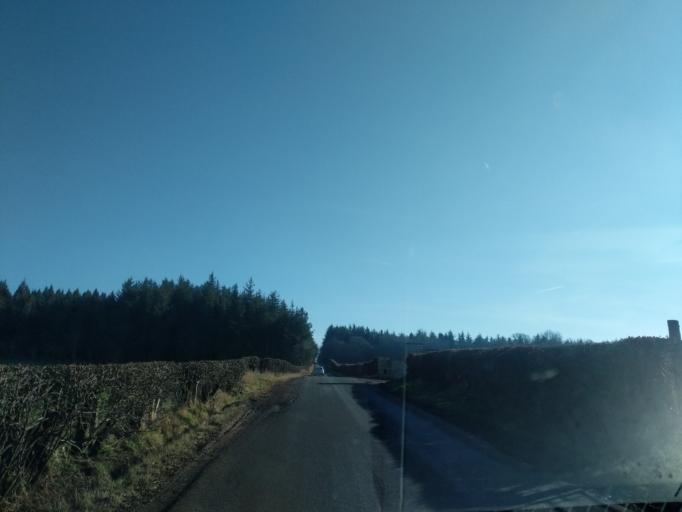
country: GB
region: Scotland
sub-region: South Lanarkshire
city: Carluke
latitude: 55.6943
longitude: -3.8480
